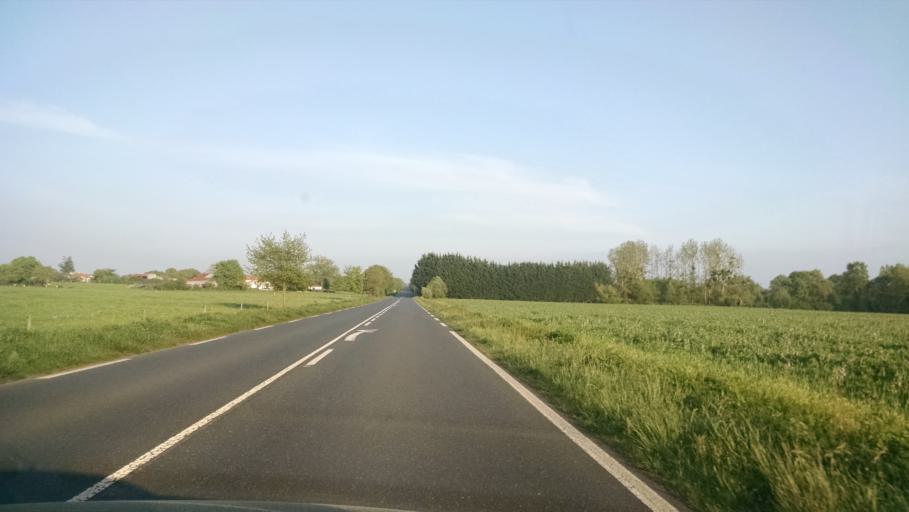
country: FR
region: Pays de la Loire
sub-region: Departement de la Loire-Atlantique
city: Boussay
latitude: 47.0677
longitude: -1.2078
